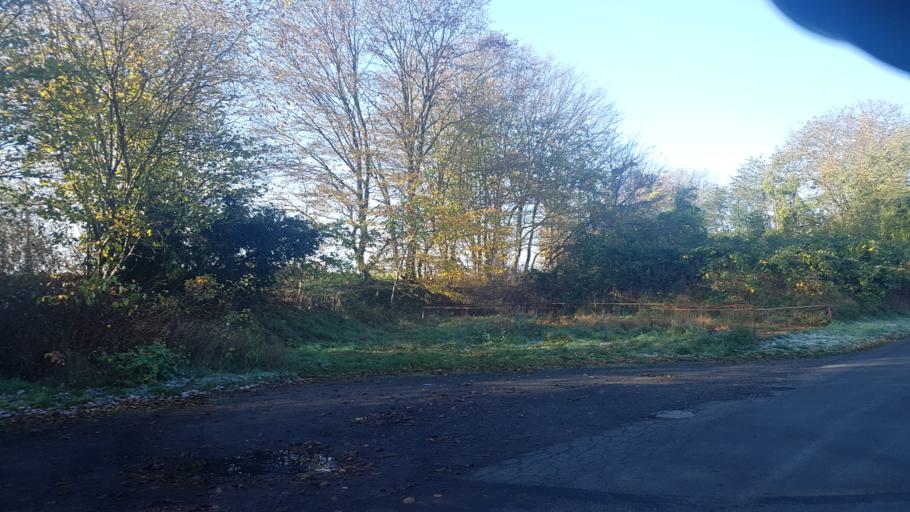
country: DE
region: Saxony
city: Dahlen
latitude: 51.3613
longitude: 12.9982
